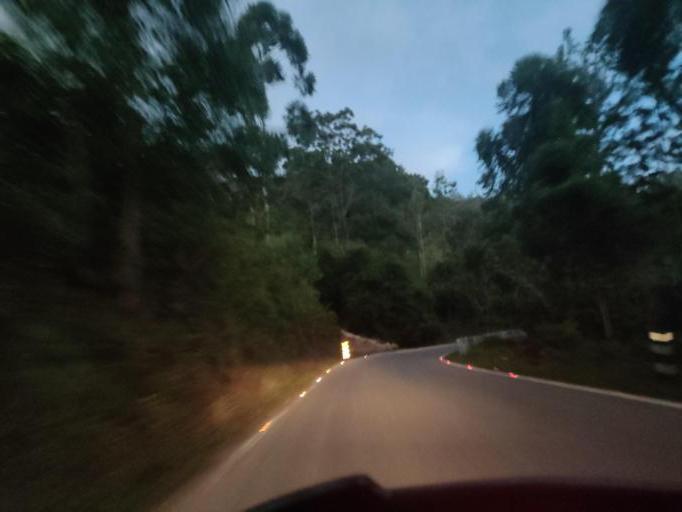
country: IN
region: Tamil Nadu
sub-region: Dindigul
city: Kodaikanal
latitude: 10.2805
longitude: 77.5331
